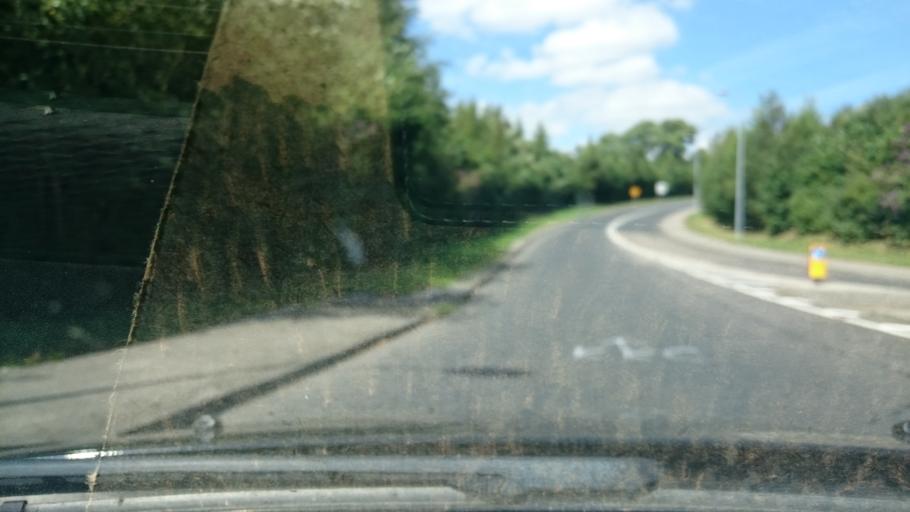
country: IE
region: Leinster
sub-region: Kilkenny
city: Graiguenamanagh
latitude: 52.5375
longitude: -6.9636
